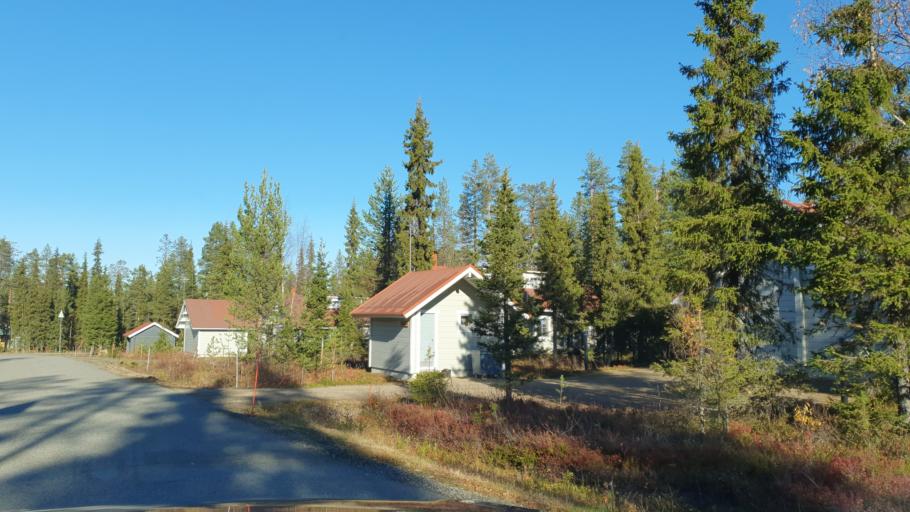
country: FI
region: Lapland
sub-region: Tunturi-Lappi
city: Kolari
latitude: 67.5984
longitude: 24.1801
